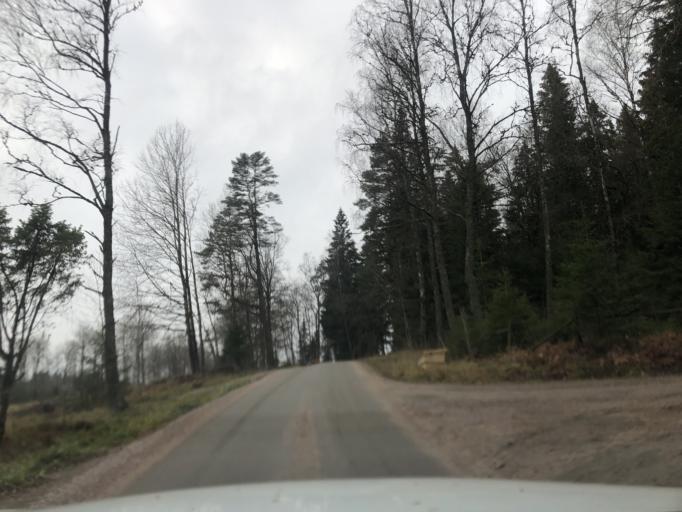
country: SE
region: Vaestra Goetaland
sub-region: Ulricehamns Kommun
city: Ulricehamn
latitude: 57.8588
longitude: 13.6141
